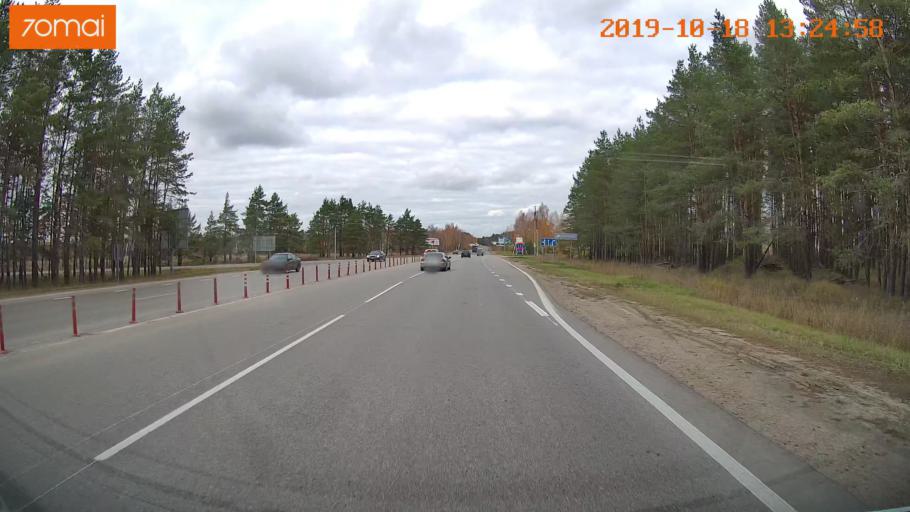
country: RU
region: Rjazan
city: Polyany
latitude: 54.7385
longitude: 39.8411
